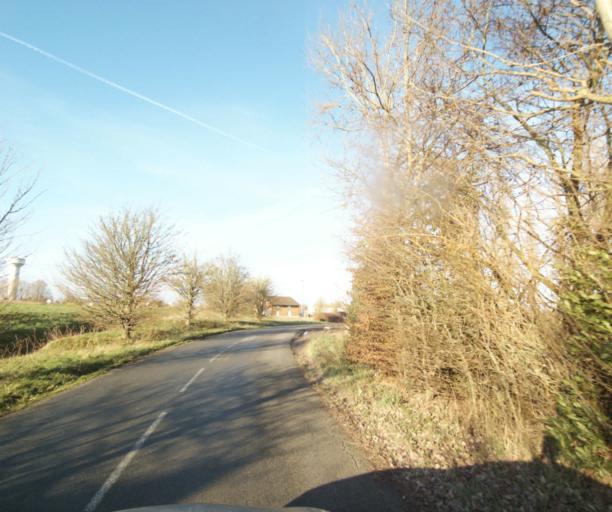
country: FR
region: Nord-Pas-de-Calais
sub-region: Departement du Nord
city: Curgies
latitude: 50.3324
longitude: 3.5914
